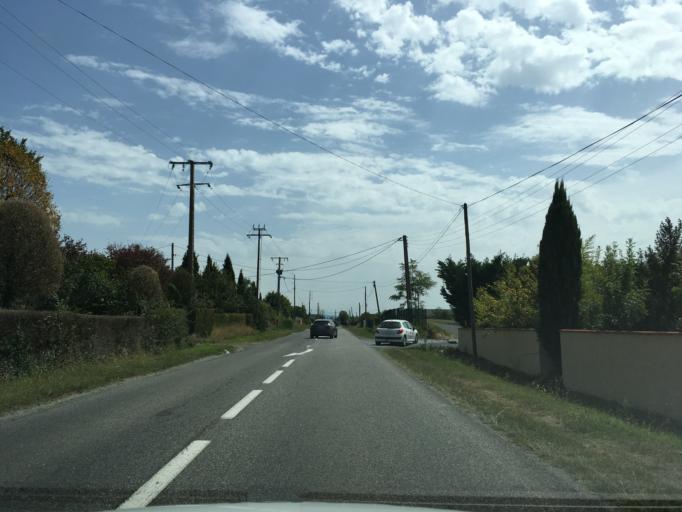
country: FR
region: Midi-Pyrenees
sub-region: Departement du Tarn
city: Castres
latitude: 43.6222
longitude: 2.2206
